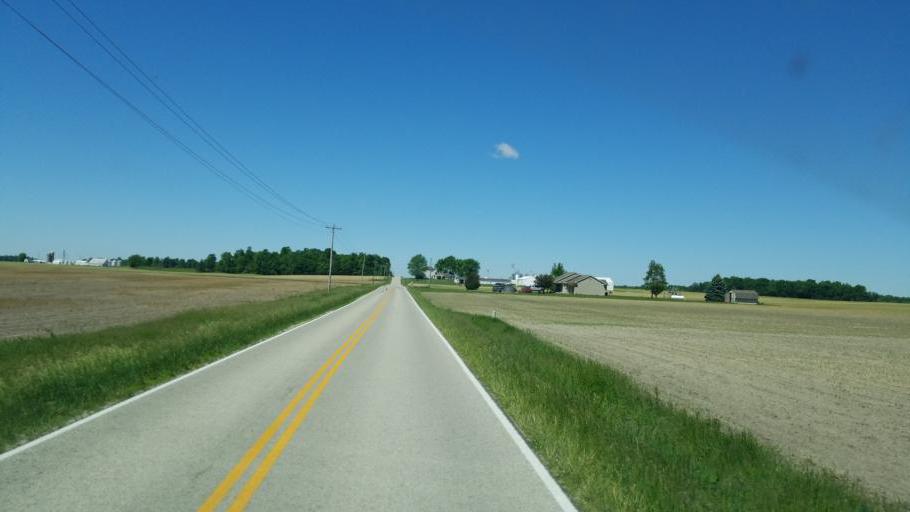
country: US
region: Ohio
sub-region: Shelby County
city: Anna
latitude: 40.3804
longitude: -84.2061
